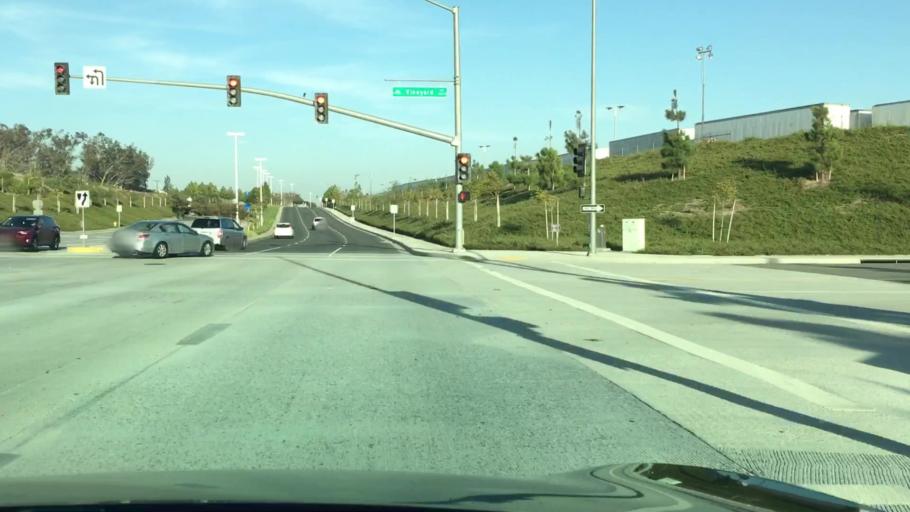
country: US
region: California
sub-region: San Bernardino County
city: Ontario
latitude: 34.0617
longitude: -117.6112
